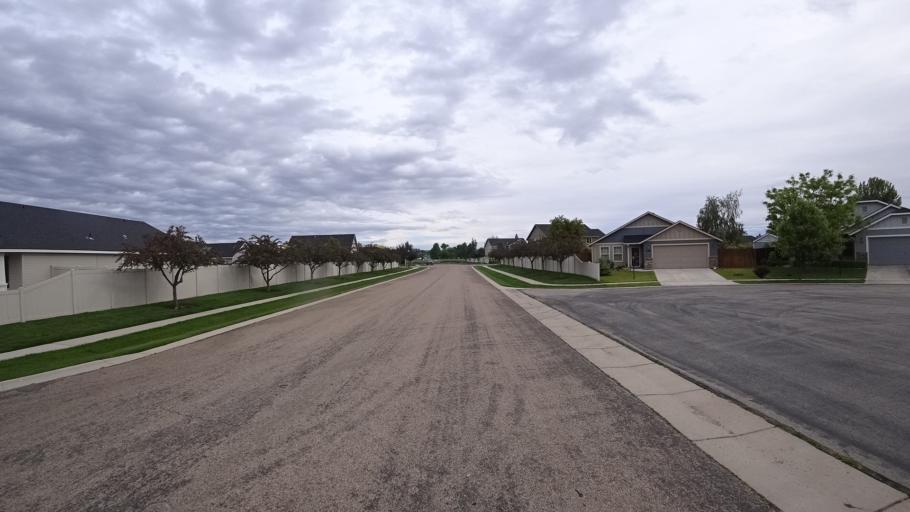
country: US
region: Idaho
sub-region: Ada County
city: Star
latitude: 43.7025
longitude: -116.5053
